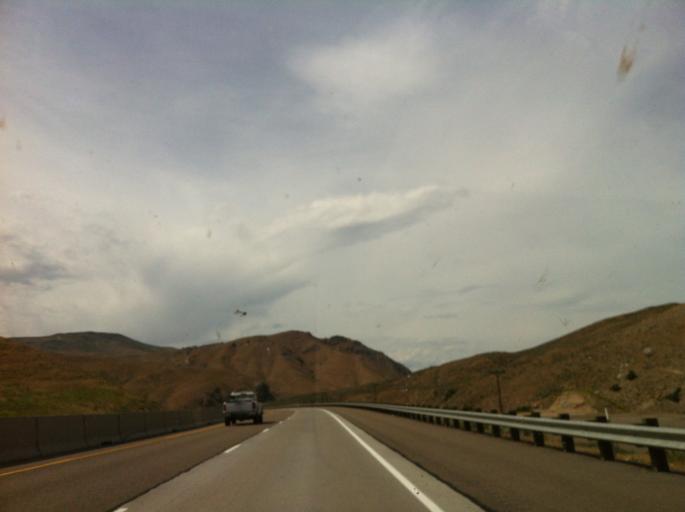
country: US
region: Idaho
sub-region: Washington County
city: Weiser
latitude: 44.3655
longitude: -117.2931
